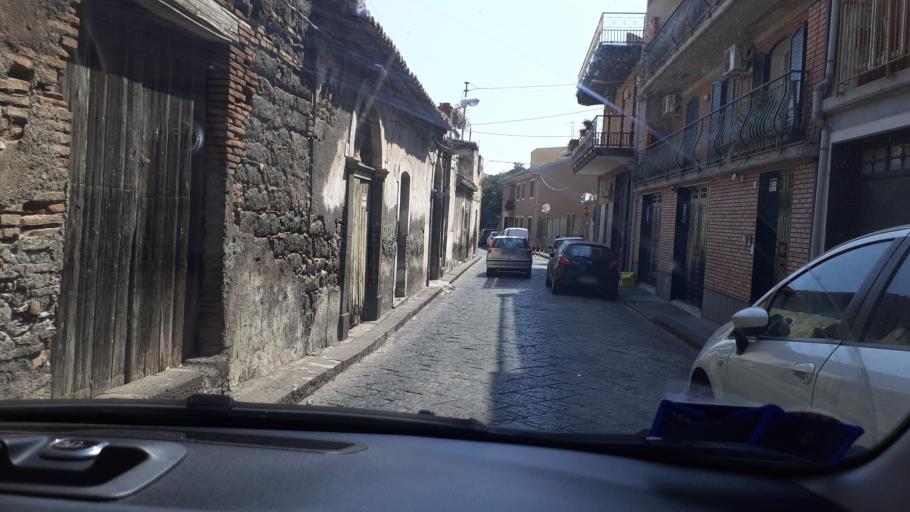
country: IT
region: Sicily
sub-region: Catania
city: Misterbianco
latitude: 37.5184
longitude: 15.0129
